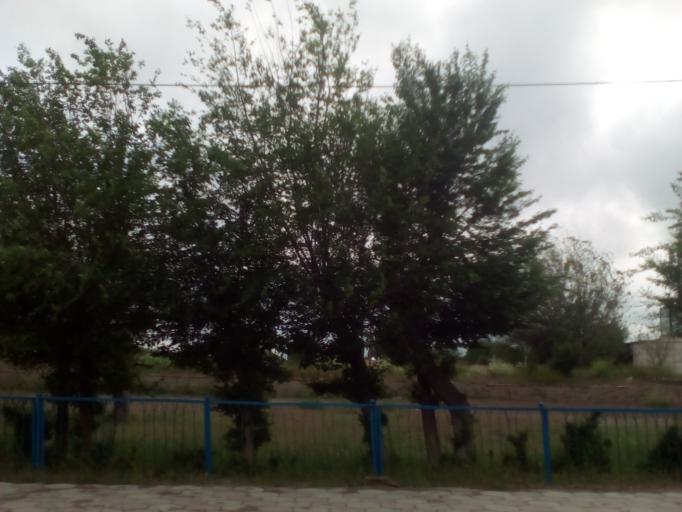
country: KZ
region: Ongtustik Qazaqstan
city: Sholaqqkorghan
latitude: 43.7587
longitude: 69.1887
